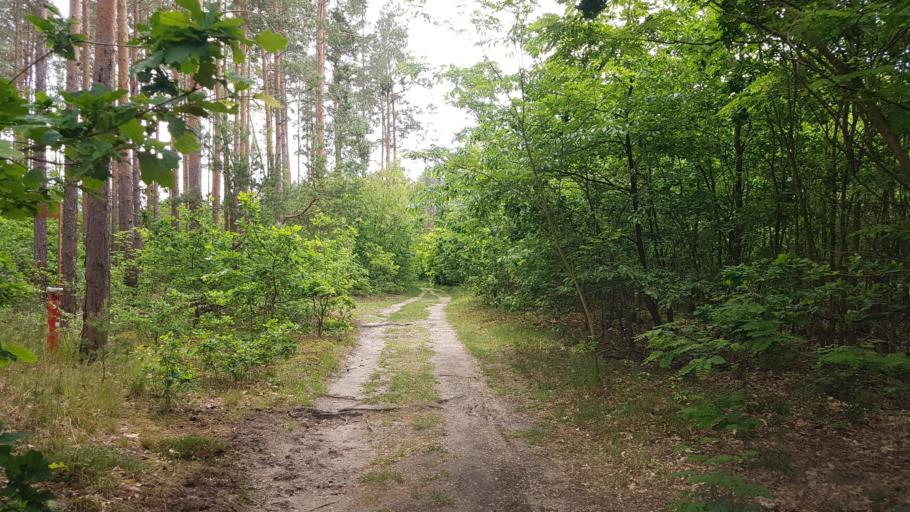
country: DE
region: Brandenburg
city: Altdobern
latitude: 51.6469
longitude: 14.0135
